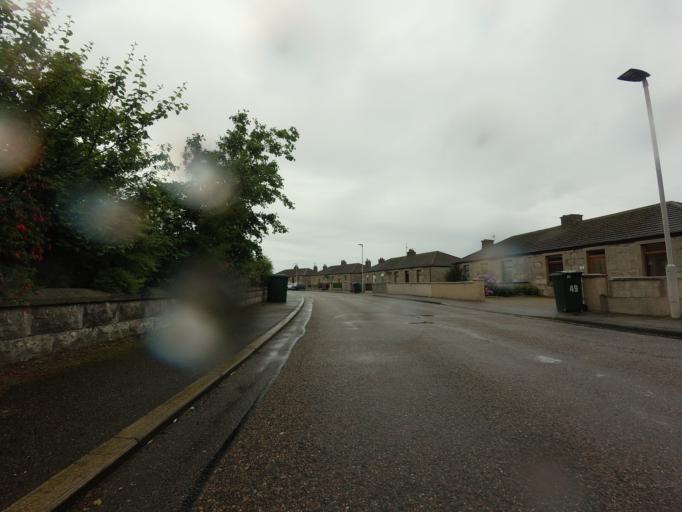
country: GB
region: Scotland
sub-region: Moray
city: Buckie
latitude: 57.6773
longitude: -2.9530
